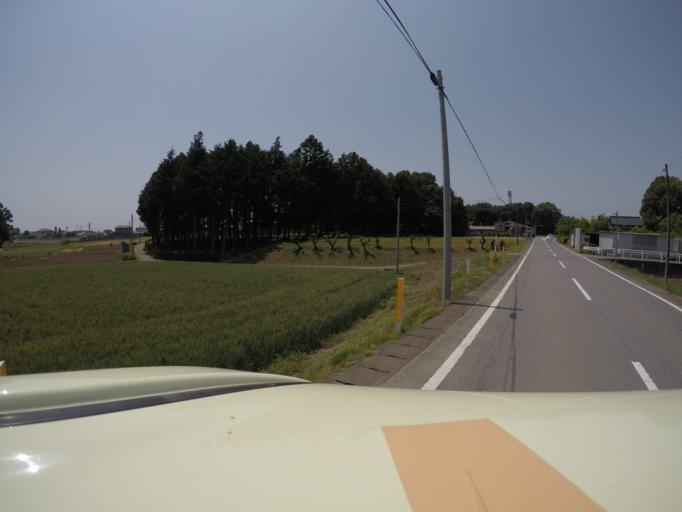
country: JP
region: Ibaraki
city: Iwai
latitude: 36.0383
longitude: 139.9384
